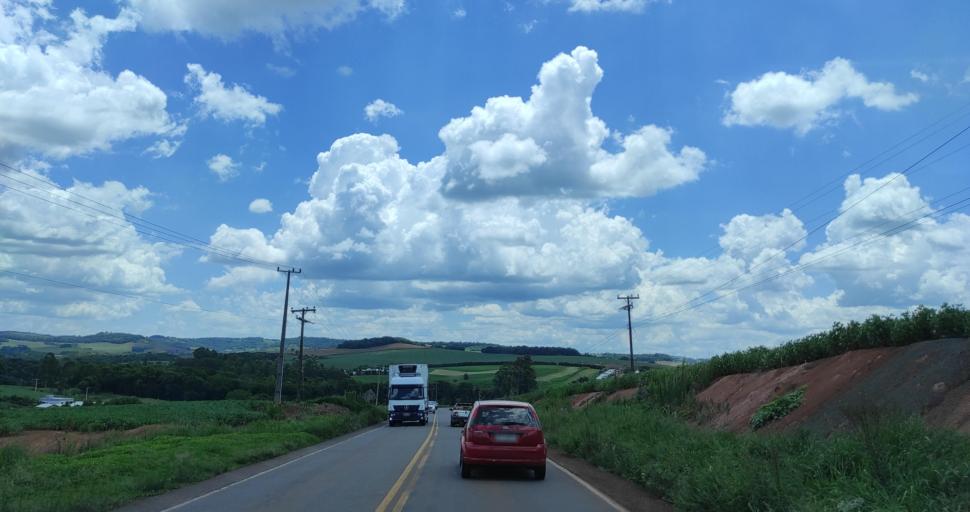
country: BR
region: Santa Catarina
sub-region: Xanxere
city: Xanxere
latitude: -26.7542
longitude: -52.4025
